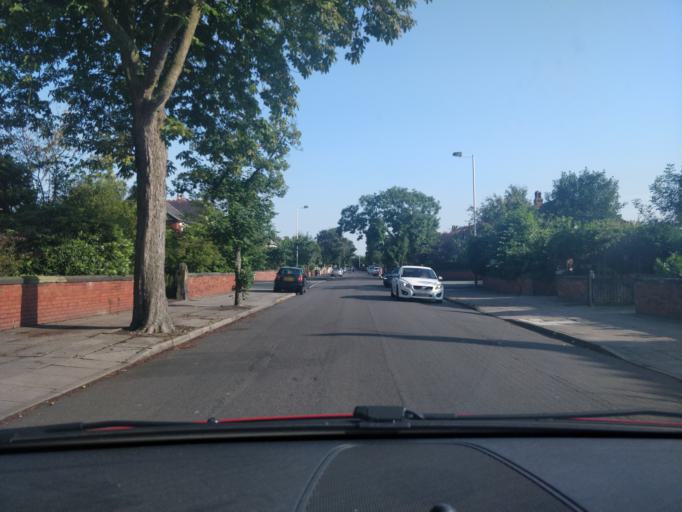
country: GB
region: England
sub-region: Sefton
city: Southport
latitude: 53.6524
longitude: -2.9744
